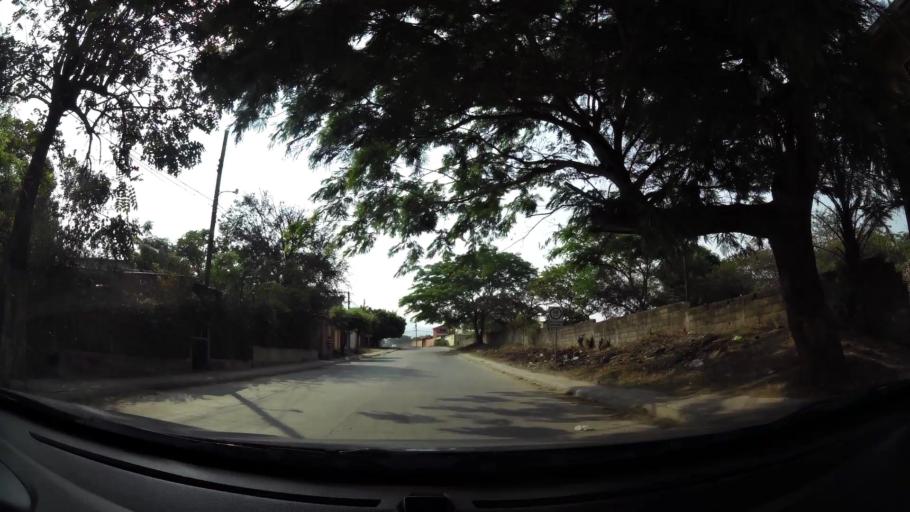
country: HN
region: Comayagua
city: Comayagua
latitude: 14.4538
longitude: -87.6260
